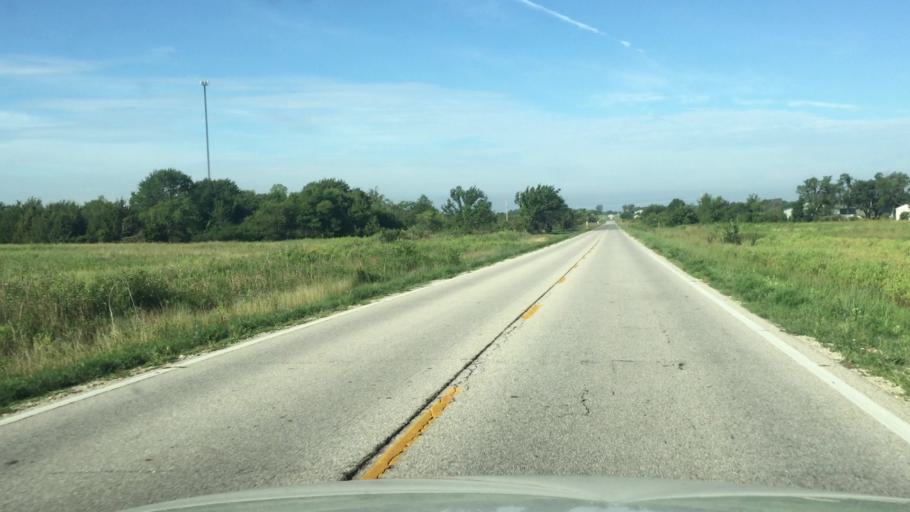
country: US
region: Kansas
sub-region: Anderson County
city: Garnett
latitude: 38.1743
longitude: -95.2770
